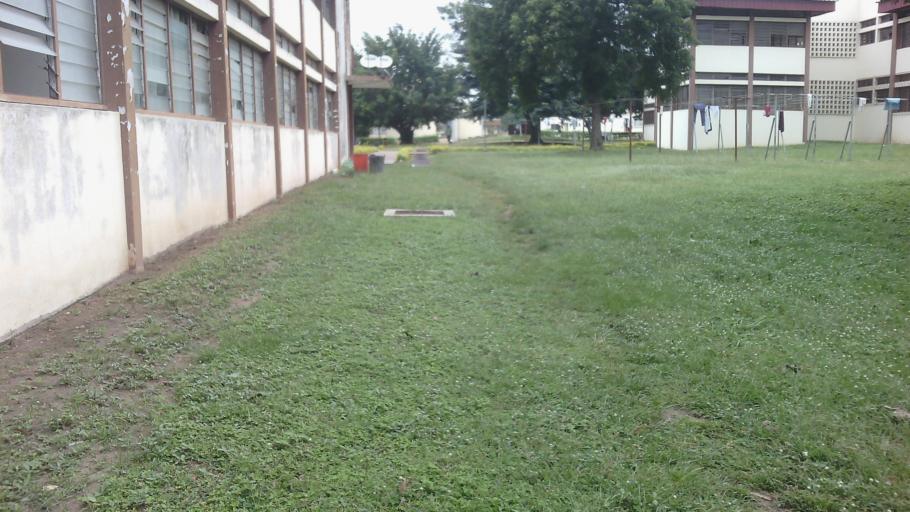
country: CI
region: Vallee du Bandama
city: Bouake
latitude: 7.6853
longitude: -5.0682
